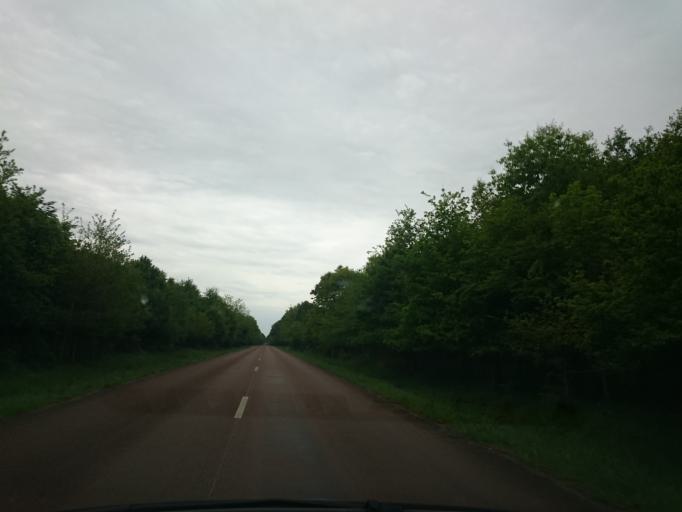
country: FR
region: Centre
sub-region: Departement du Loir-et-Cher
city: Muides-sur-Loire
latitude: 47.6520
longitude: 1.5307
